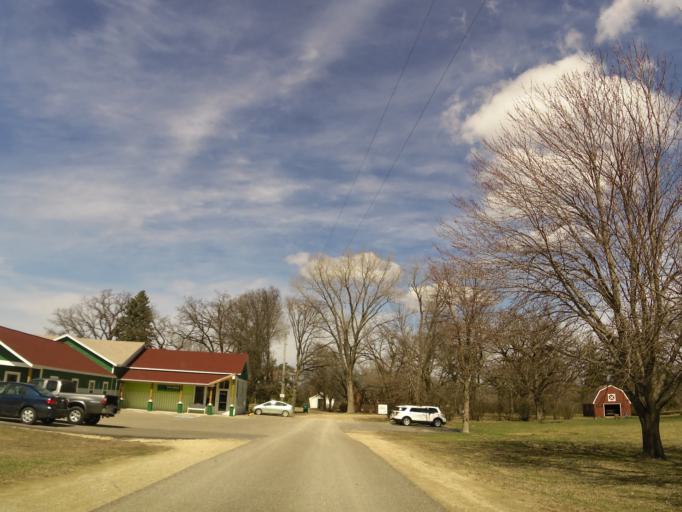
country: US
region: Minnesota
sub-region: Goodhue County
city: Cannon Falls
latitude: 44.4930
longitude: -92.9140
